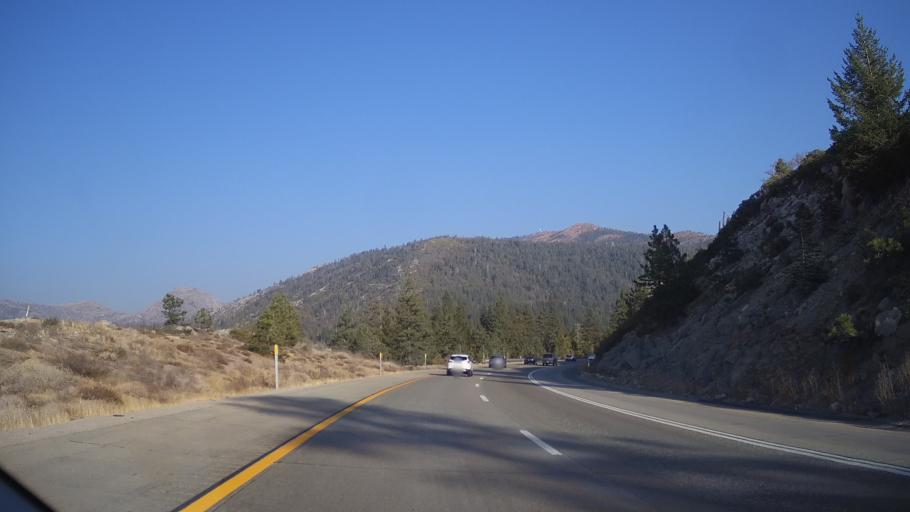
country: US
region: California
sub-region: Sierra County
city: Downieville
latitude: 39.3298
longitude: -120.5891
